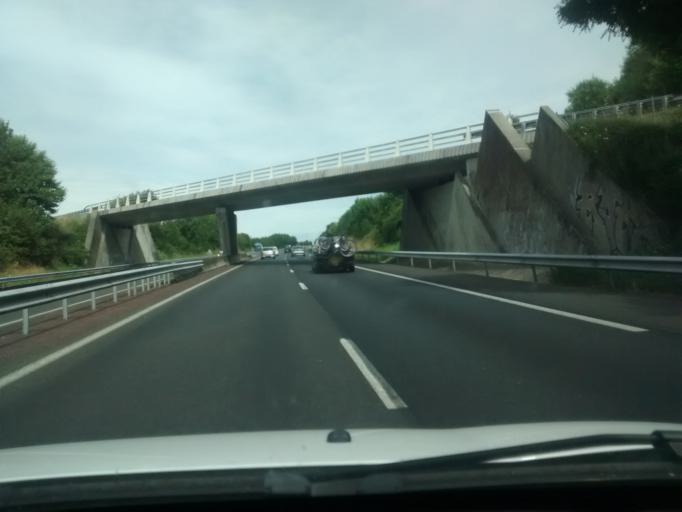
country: FR
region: Lower Normandy
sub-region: Departement de la Manche
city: Saint-James
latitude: 48.5564
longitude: -1.3411
